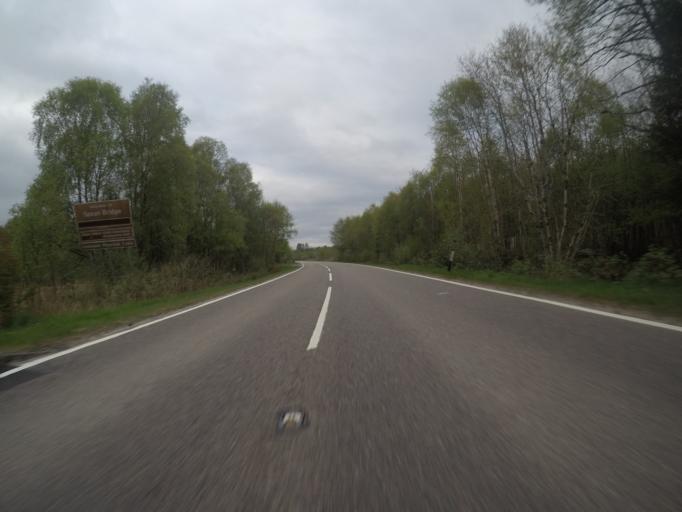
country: GB
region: Scotland
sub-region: Highland
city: Spean Bridge
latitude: 56.8954
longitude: -4.9047
